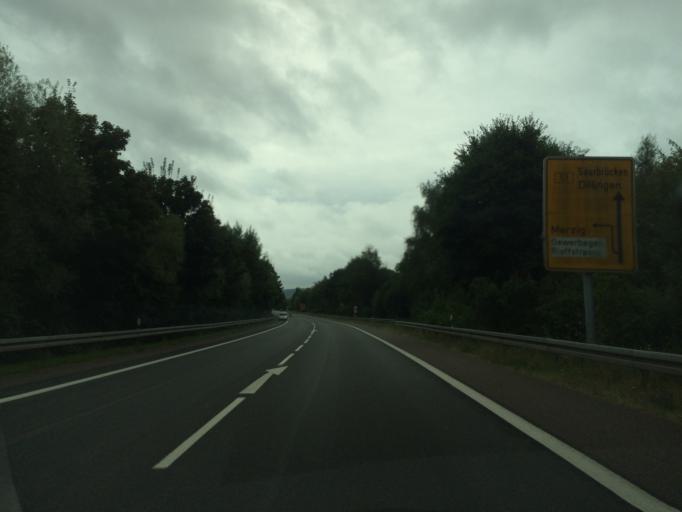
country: DE
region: Saarland
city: Merzig
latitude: 49.4331
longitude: 6.6307
